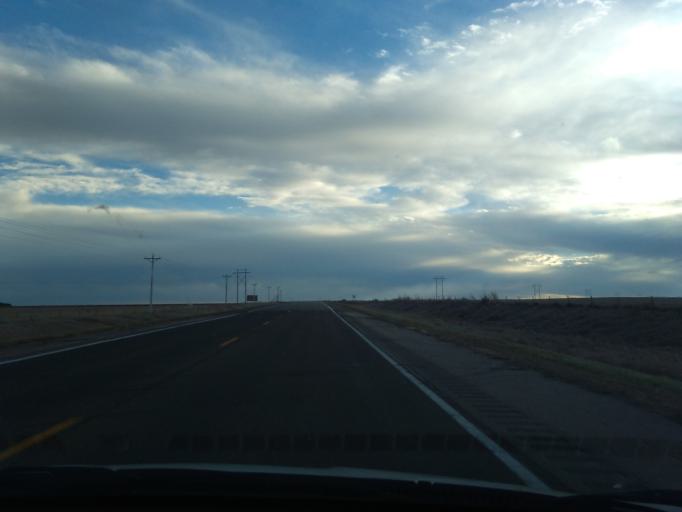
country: US
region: Nebraska
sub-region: Phelps County
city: Holdrege
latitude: 40.3835
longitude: -99.3701
